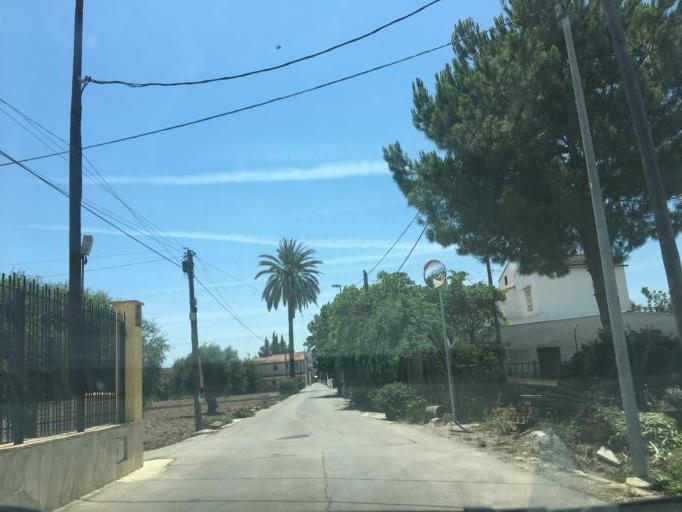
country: ES
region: Murcia
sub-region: Murcia
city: Santomera
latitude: 38.0188
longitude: -1.0559
